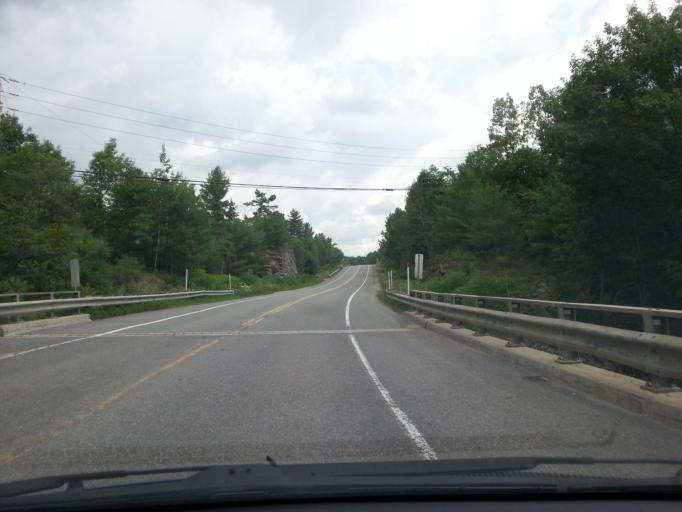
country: CA
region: Quebec
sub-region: Outaouais
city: Val-des-Monts
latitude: 45.6420
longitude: -75.6278
